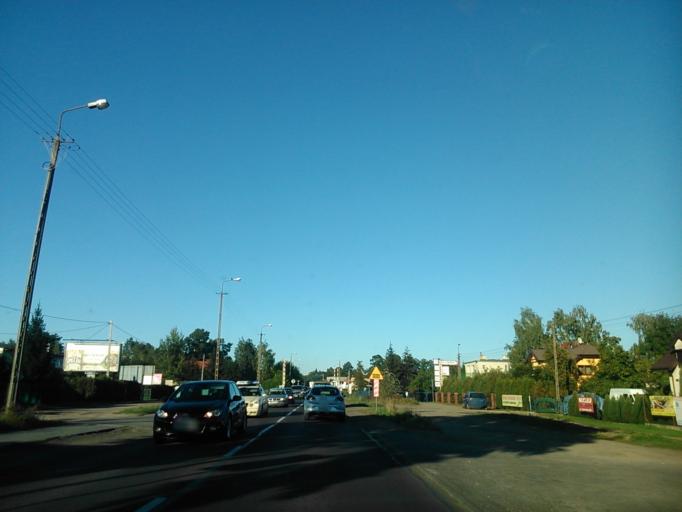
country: PL
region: Kujawsko-Pomorskie
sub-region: Powiat torunski
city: Lubicz Dolny
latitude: 53.0424
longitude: 18.6989
